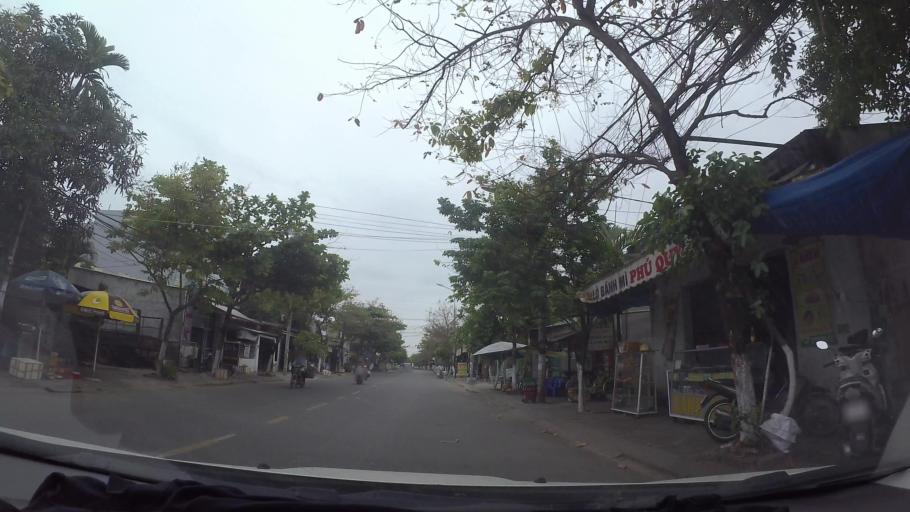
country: VN
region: Da Nang
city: Lien Chieu
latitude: 16.0650
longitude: 108.1501
